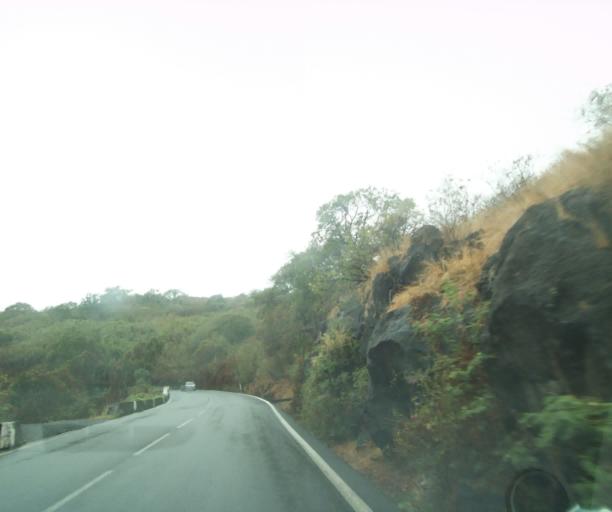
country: RE
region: Reunion
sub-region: Reunion
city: Saint-Paul
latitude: -21.0162
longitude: 55.2822
